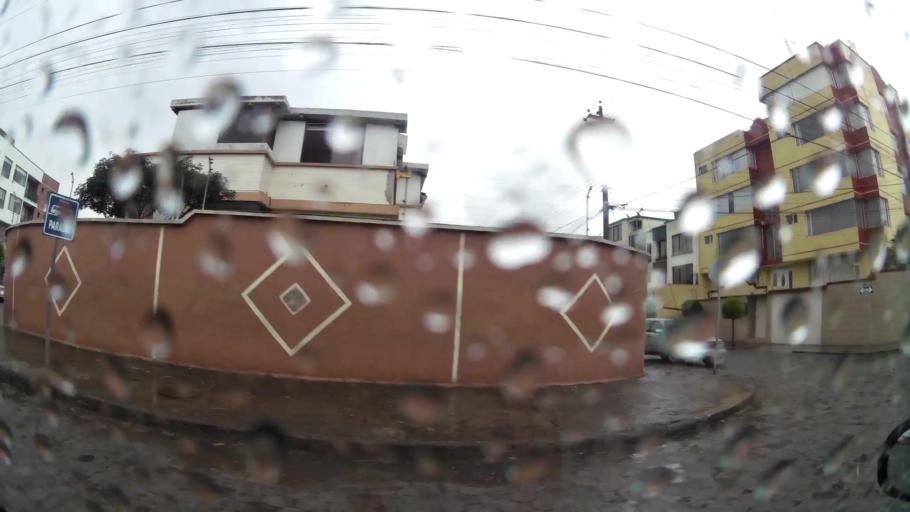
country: EC
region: Pichincha
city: Quito
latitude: -0.1566
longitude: -78.4637
